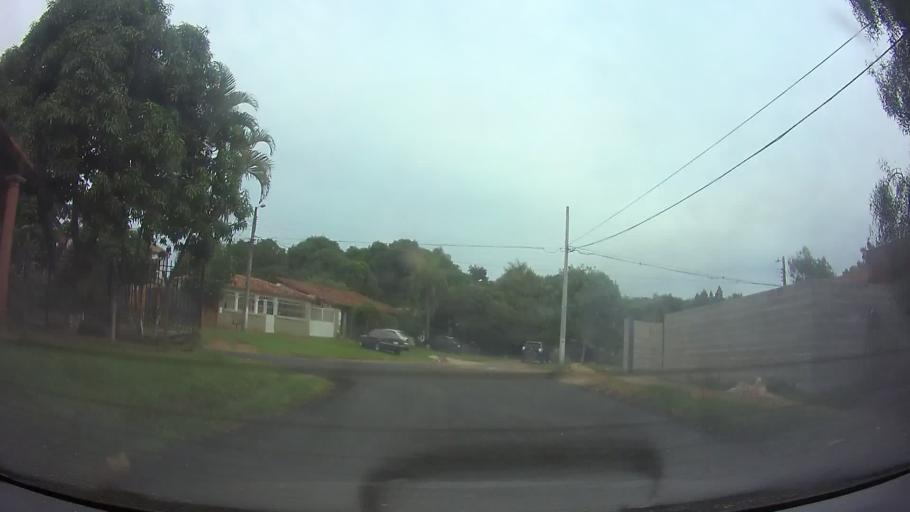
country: PY
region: Central
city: San Lorenzo
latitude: -25.2629
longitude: -57.4833
